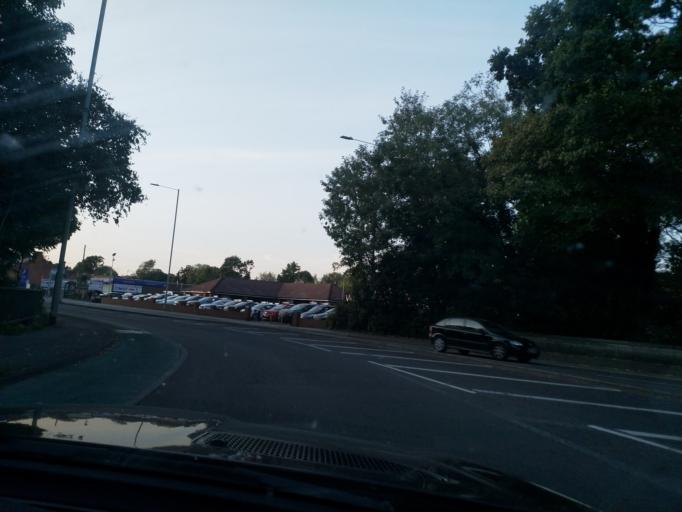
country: GB
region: England
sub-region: Kent
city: Leysdown-on-Sea
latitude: 51.4182
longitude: 0.8525
